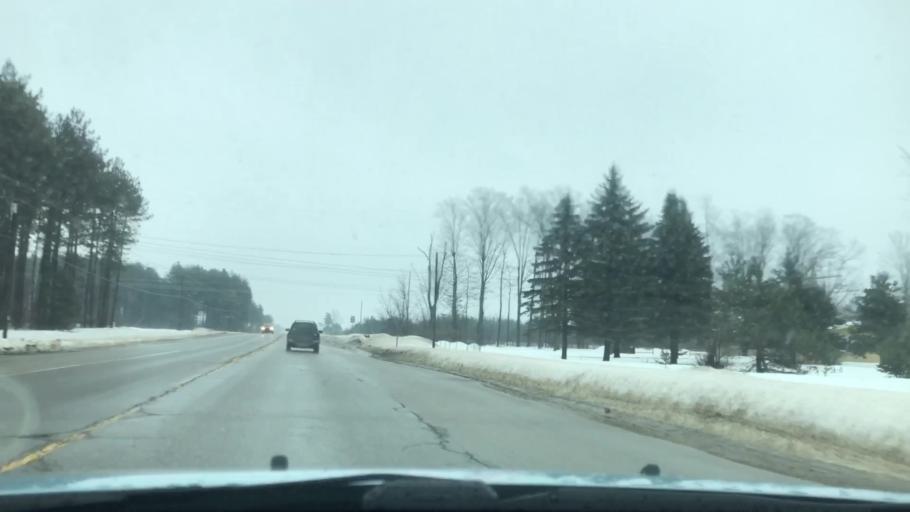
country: US
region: Michigan
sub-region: Otsego County
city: Gaylord
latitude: 45.0276
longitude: -84.7352
